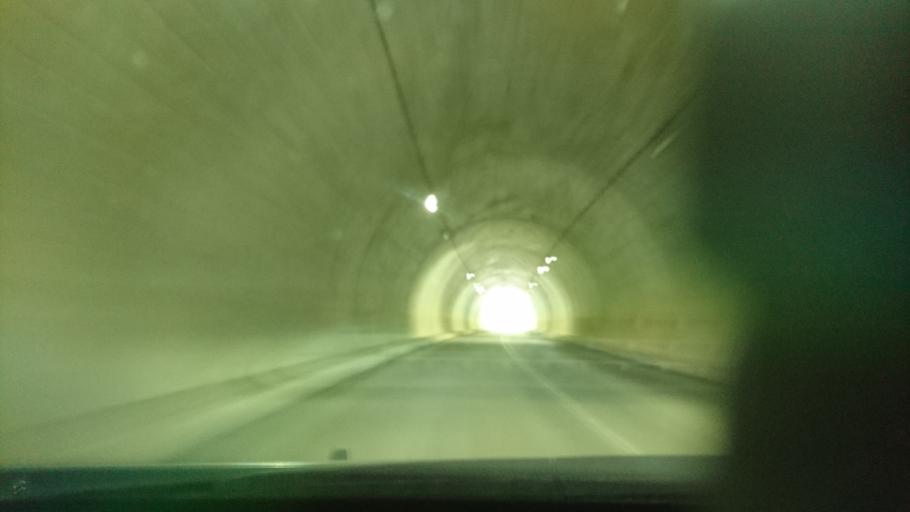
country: JP
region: Iwate
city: Ichinoseki
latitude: 38.9026
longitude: 140.9038
